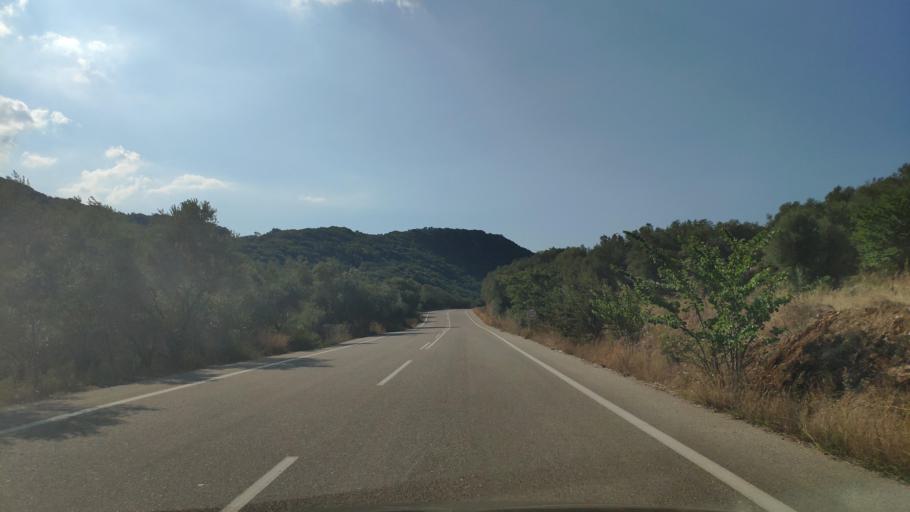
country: GR
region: West Greece
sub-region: Nomos Aitolias kai Akarnanias
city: Stanos
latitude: 38.7748
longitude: 21.1520
